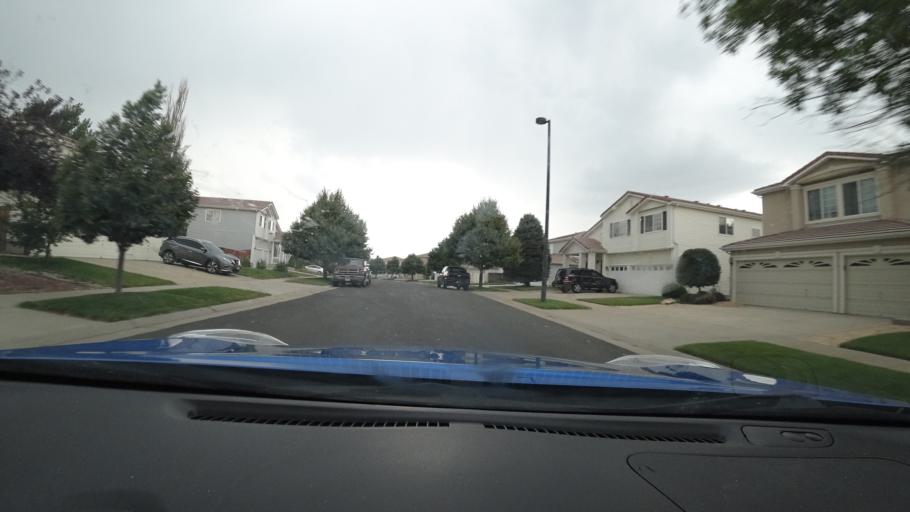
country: US
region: Colorado
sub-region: Adams County
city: Aurora
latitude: 39.7836
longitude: -104.7452
